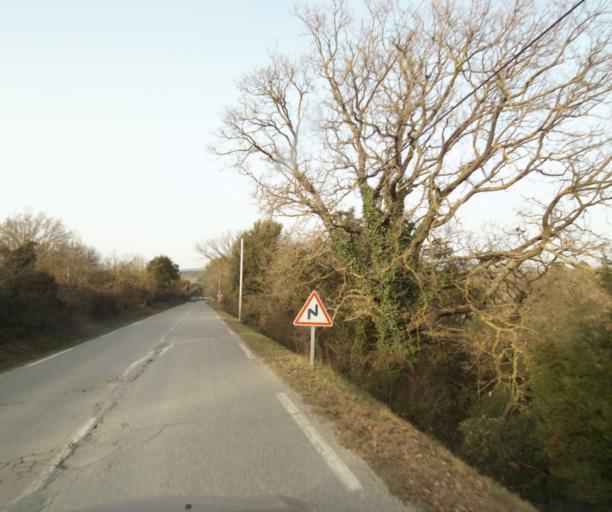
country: FR
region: Provence-Alpes-Cote d'Azur
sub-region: Departement des Bouches-du-Rhone
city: Eguilles
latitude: 43.5814
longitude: 5.3656
